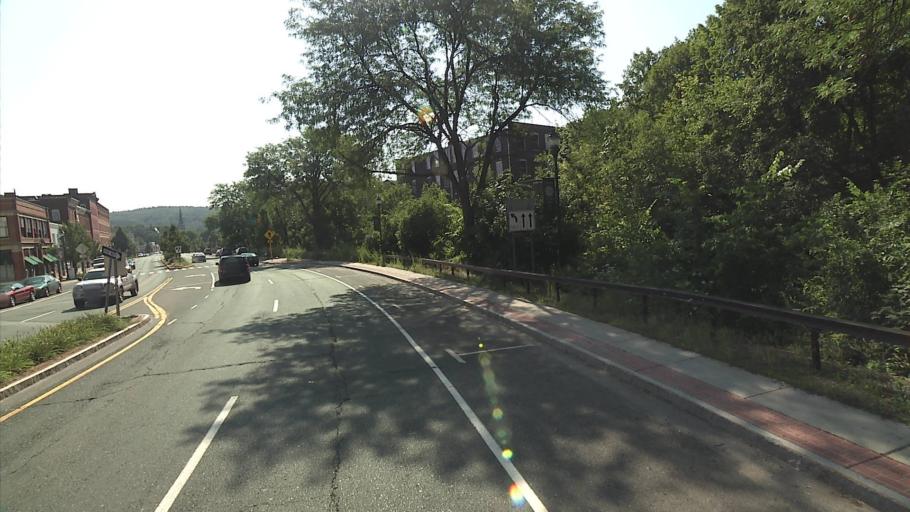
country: US
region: Connecticut
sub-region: Litchfield County
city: Winsted
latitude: 41.9208
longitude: -73.0728
